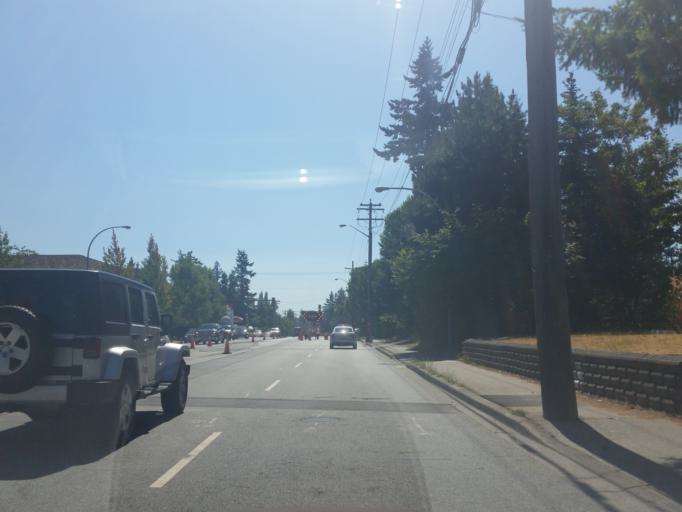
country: CA
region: British Columbia
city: Langley
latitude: 49.1058
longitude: -122.6689
